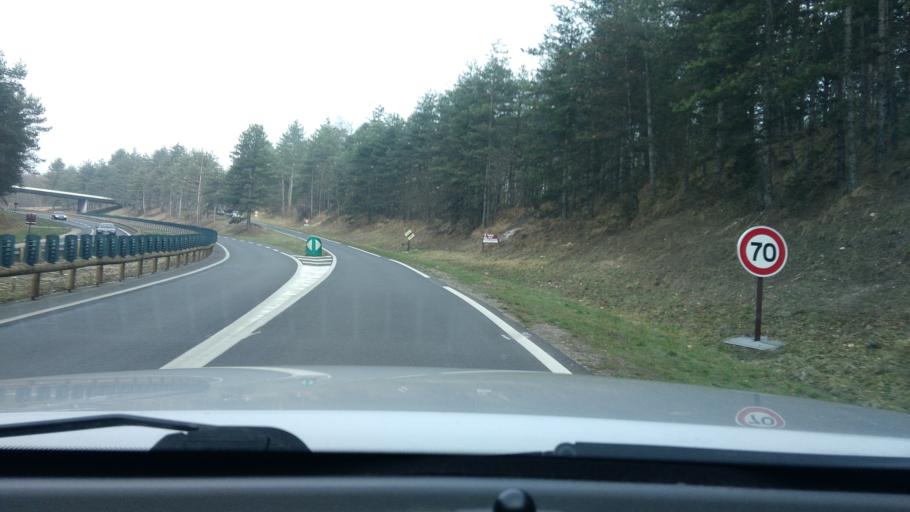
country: FR
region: Ile-de-France
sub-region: Departement de Seine-et-Marne
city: Avon
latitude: 48.4229
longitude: 2.7103
